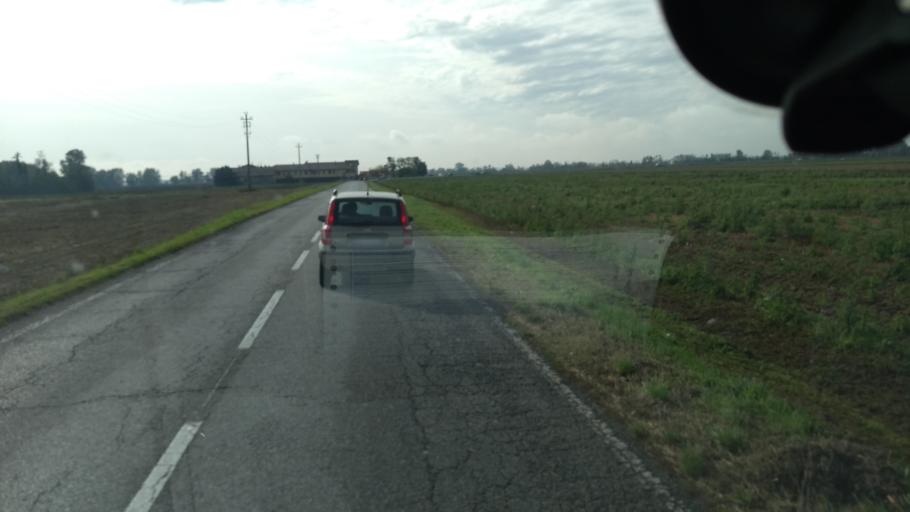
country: IT
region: Lombardy
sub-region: Provincia di Bergamo
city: Cologno al Serio
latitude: 45.5658
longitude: 9.6934
